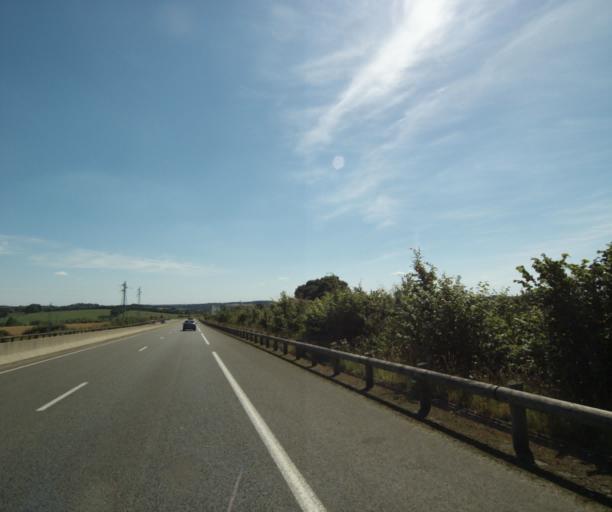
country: FR
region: Pays de la Loire
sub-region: Departement de la Mayenne
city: Montigne-le-Brillant
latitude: 48.0441
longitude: -0.8000
